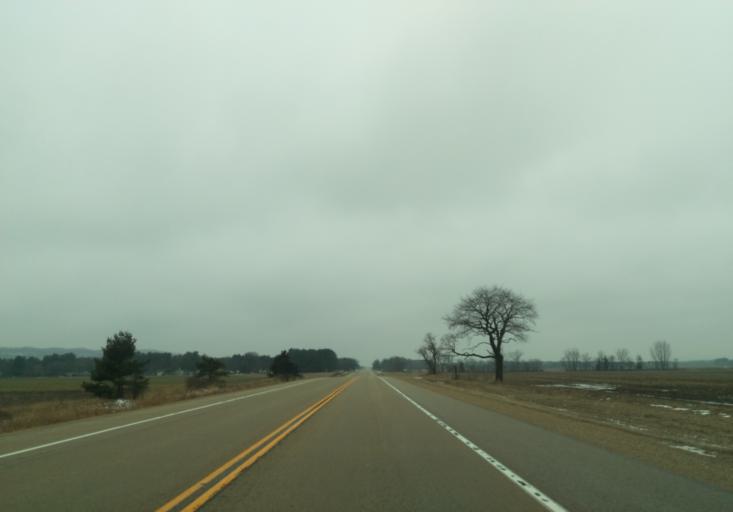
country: US
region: Wisconsin
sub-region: Sauk County
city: Spring Green
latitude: 43.1616
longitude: -89.9694
